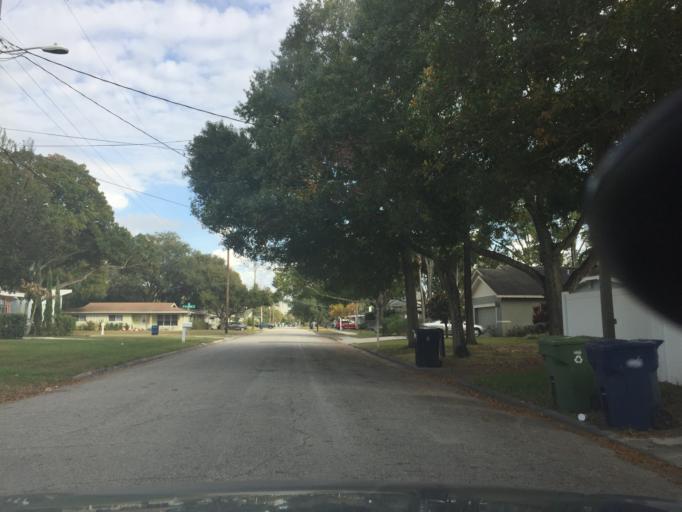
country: US
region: Florida
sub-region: Hillsborough County
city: Tampa
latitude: 27.9472
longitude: -82.4971
